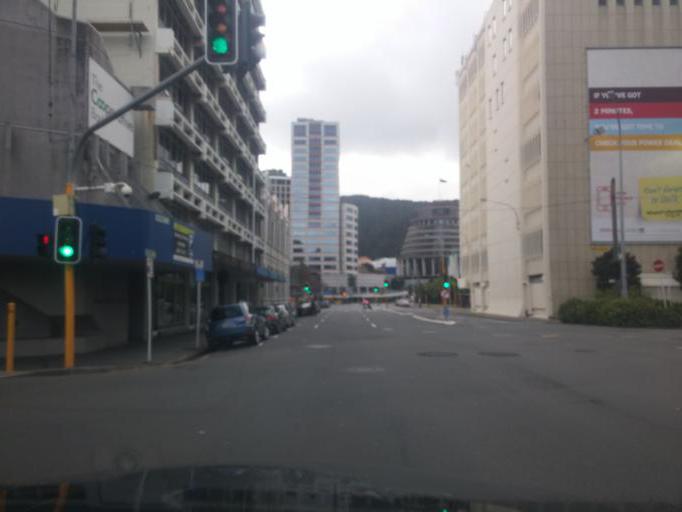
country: NZ
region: Wellington
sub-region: Wellington City
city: Wellington
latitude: -41.2812
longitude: 174.7784
